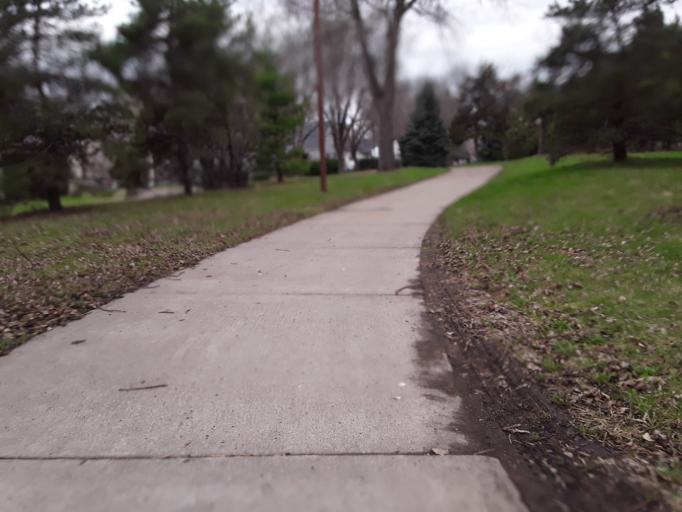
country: US
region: Nebraska
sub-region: Lancaster County
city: Lincoln
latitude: 40.8315
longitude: -96.6835
